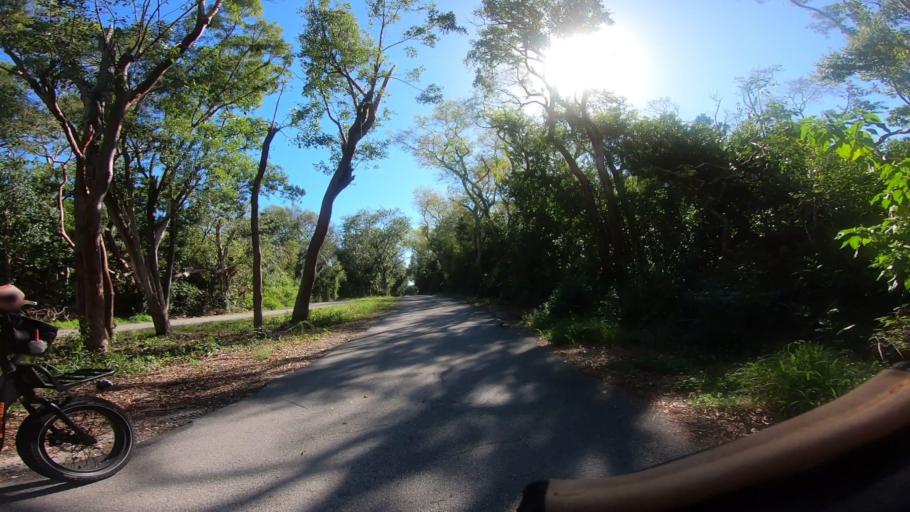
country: US
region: Florida
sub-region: Monroe County
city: Key Largo
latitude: 25.1115
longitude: -80.4268
